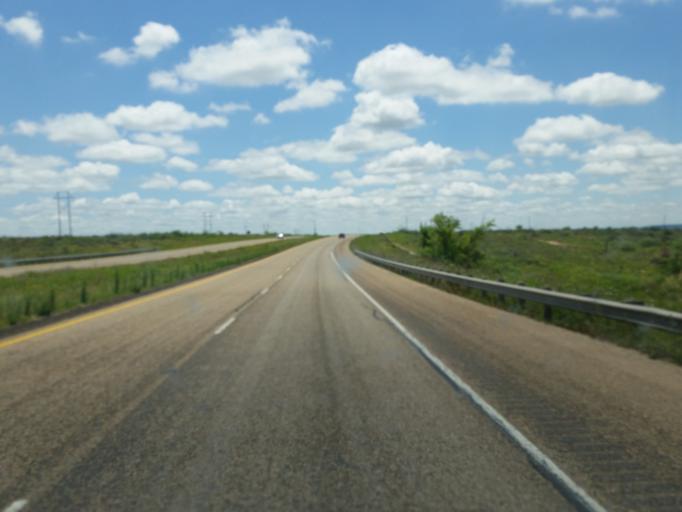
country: US
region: Texas
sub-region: Garza County
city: Post
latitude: 33.0940
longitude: -101.2494
